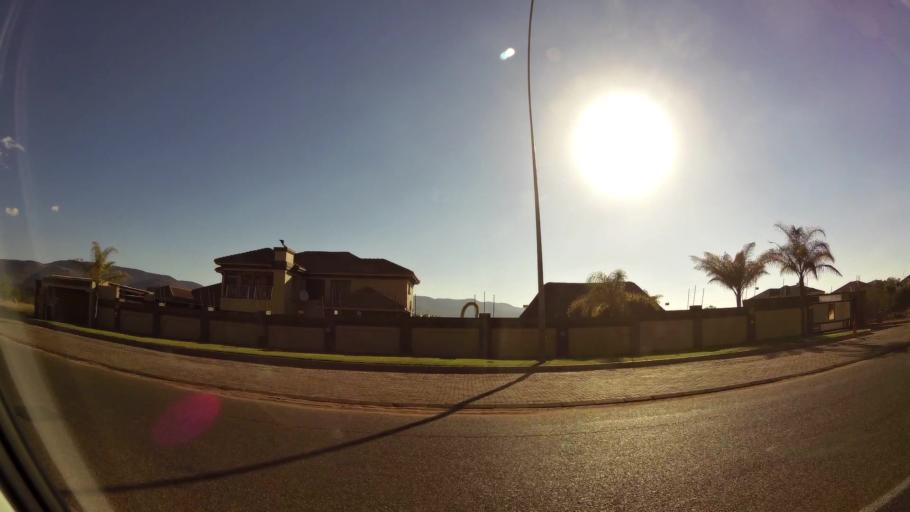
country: ZA
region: Limpopo
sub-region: Waterberg District Municipality
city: Mokopane
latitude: -24.2025
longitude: 29.0015
